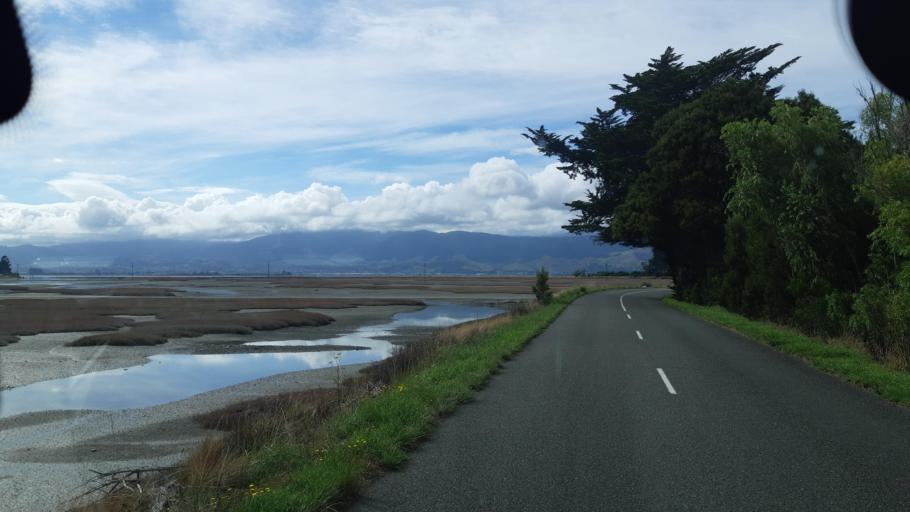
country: NZ
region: Tasman
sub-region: Tasman District
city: Richmond
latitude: -41.3014
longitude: 173.1520
